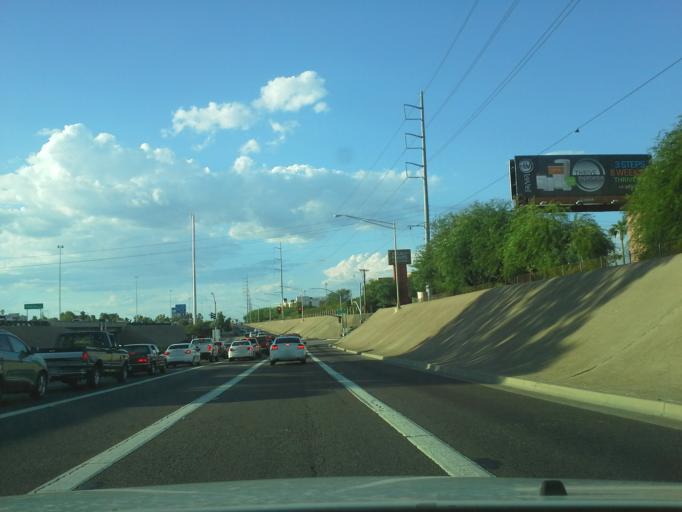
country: US
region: Arizona
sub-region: Maricopa County
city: Glendale
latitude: 33.5808
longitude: -112.1165
